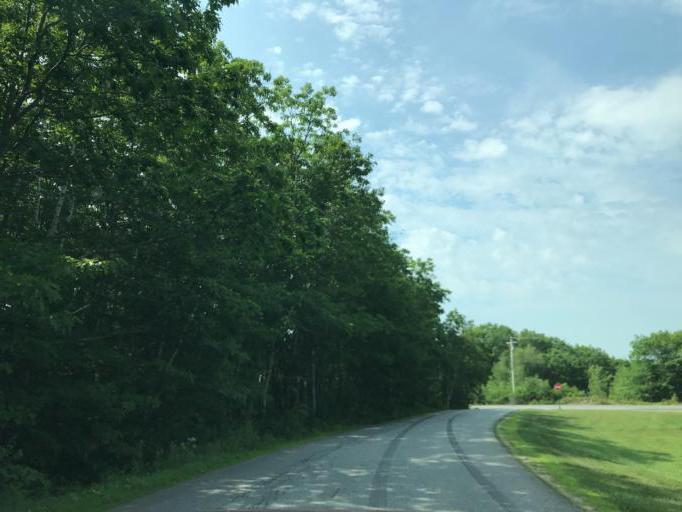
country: US
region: Maine
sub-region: Knox County
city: Hope
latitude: 44.2110
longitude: -69.1699
